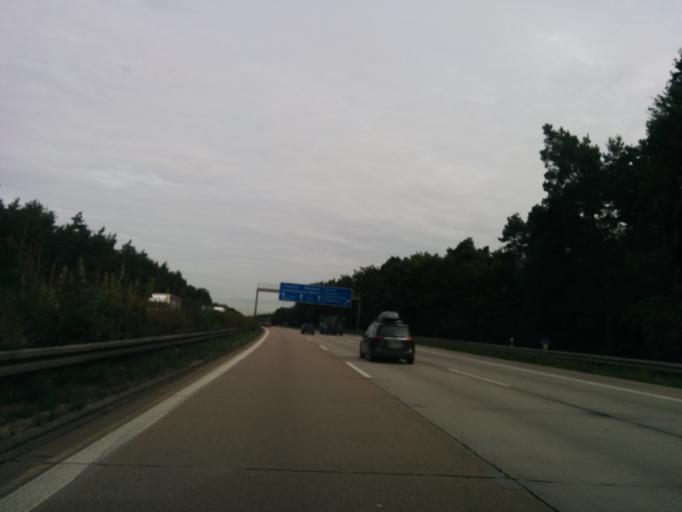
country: DE
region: Baden-Wuerttemberg
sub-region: Karlsruhe Region
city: Kronau
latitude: 49.2212
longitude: 8.6040
